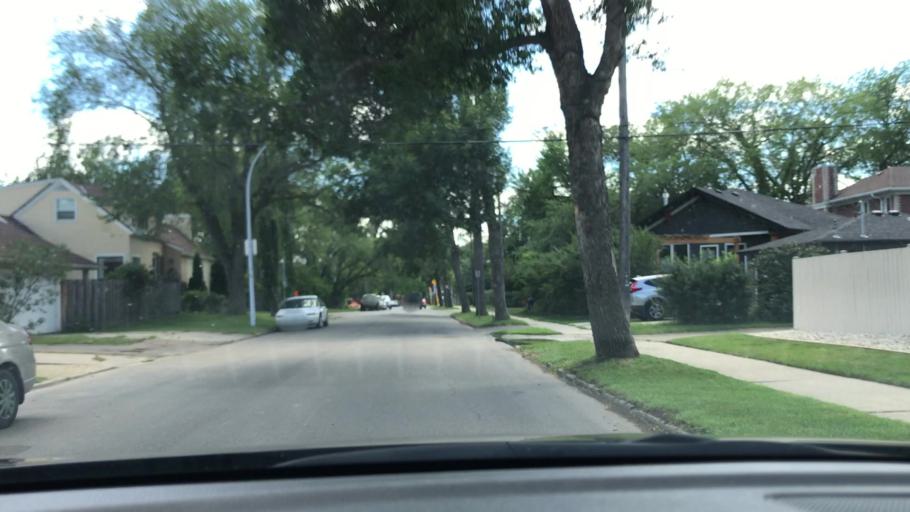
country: CA
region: Alberta
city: Edmonton
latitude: 53.5233
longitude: -113.4887
